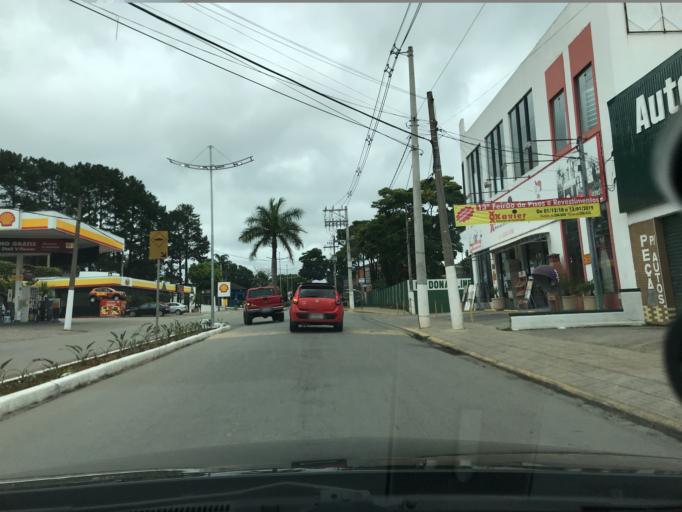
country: BR
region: Sao Paulo
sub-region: Ibiuna
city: Ibiuna
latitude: -23.6611
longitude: -47.2259
